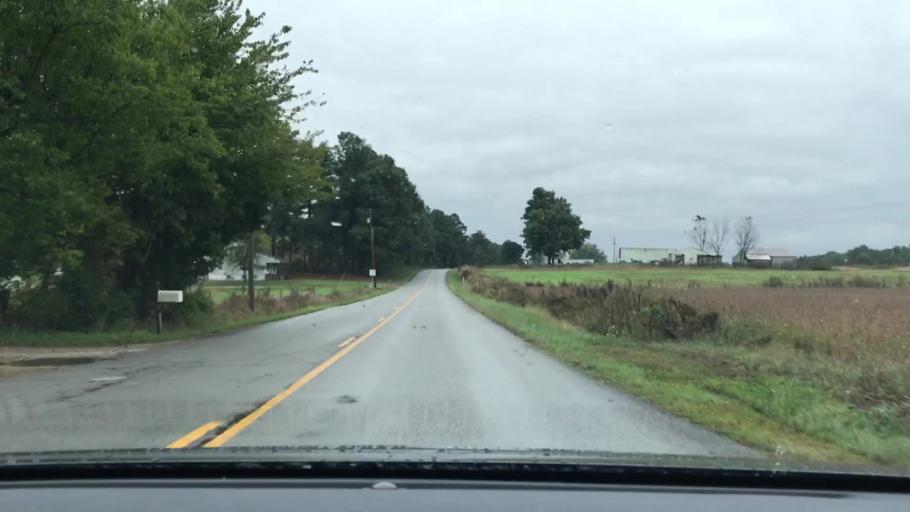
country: US
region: Kentucky
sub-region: McLean County
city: Calhoun
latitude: 37.4824
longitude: -87.2468
